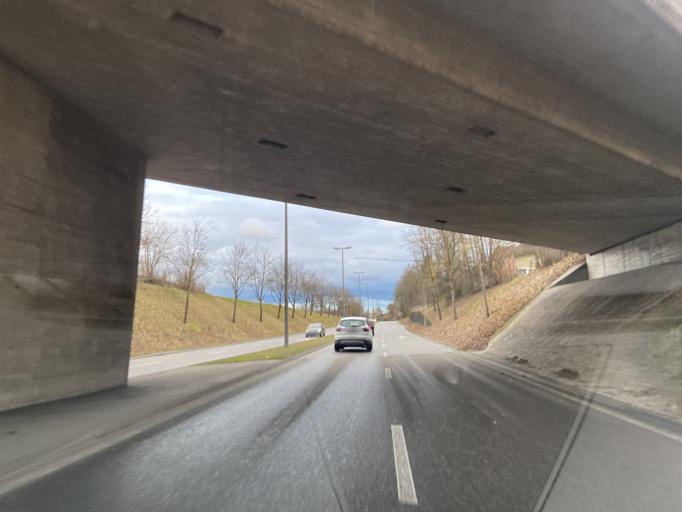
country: CH
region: Zurich
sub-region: Bezirk Winterthur
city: Wuelflingen (Kreis 6) / Lindenplatz
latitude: 47.5133
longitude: 8.6941
